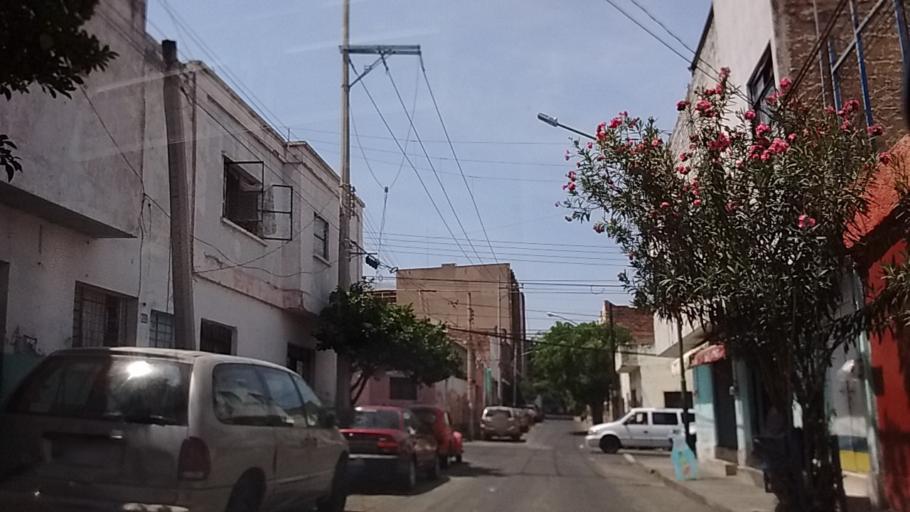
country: MX
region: Jalisco
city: Guadalajara
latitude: 20.6832
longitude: -103.3391
